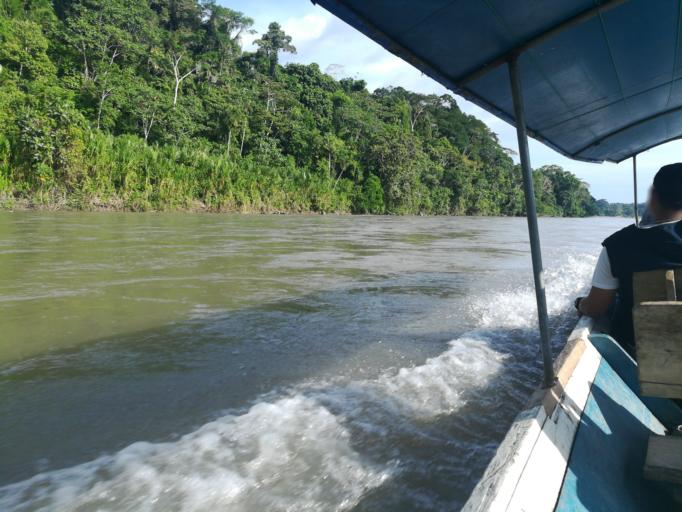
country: EC
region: Orellana
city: Boca Suno
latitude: -0.8241
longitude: -77.1989
